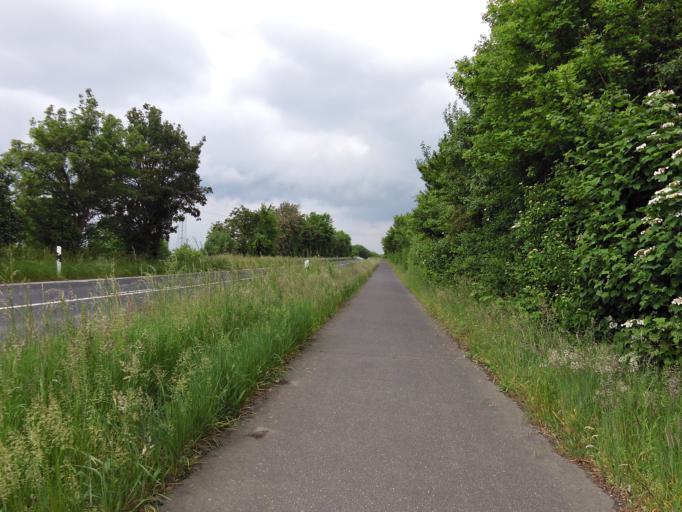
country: DE
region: North Rhine-Westphalia
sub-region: Regierungsbezirk Koln
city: Rheinbach
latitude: 50.6393
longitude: 6.9485
